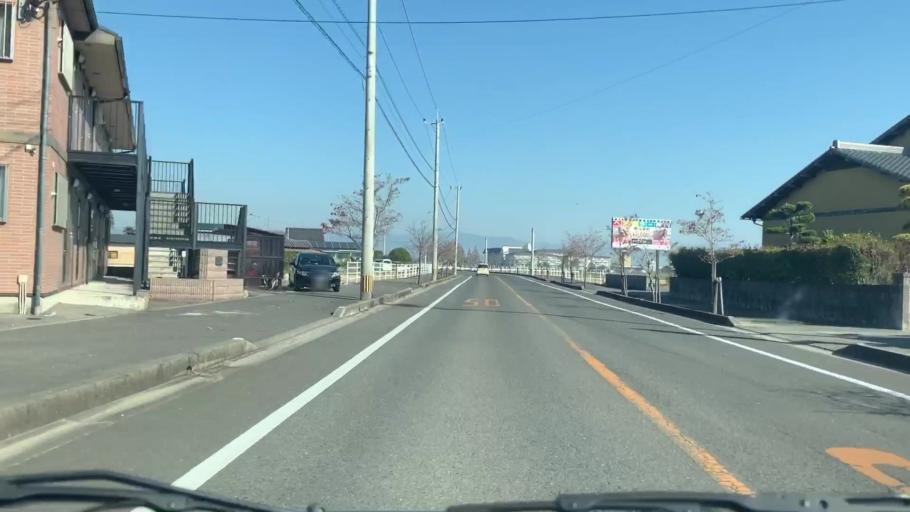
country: JP
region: Saga Prefecture
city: Saga-shi
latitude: 33.2325
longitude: 130.3125
